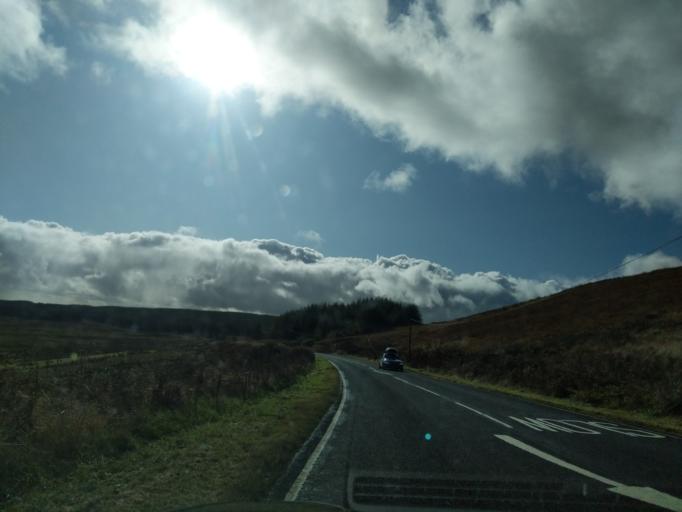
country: GB
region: Scotland
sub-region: Dumfries and Galloway
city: Moffat
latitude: 55.3926
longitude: -3.4825
